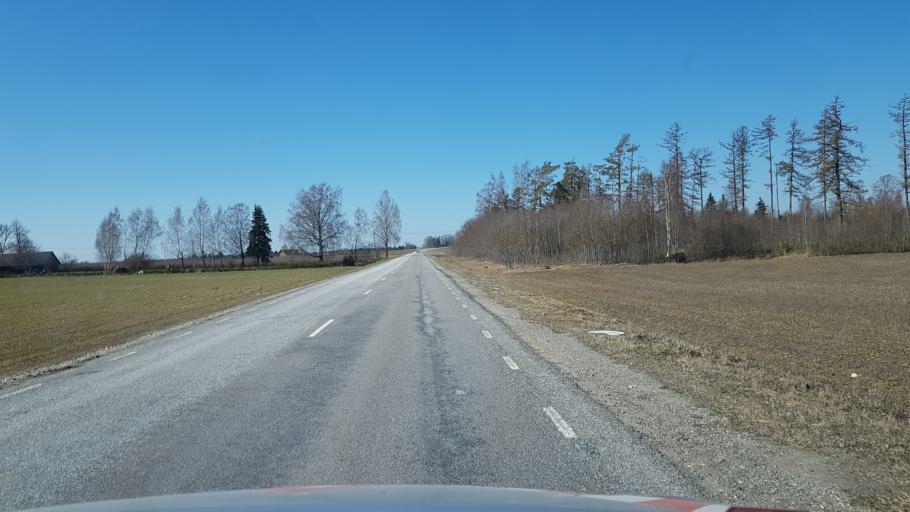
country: EE
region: Laeaene-Virumaa
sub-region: Vaeike-Maarja vald
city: Vaike-Maarja
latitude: 59.1378
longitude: 26.2453
